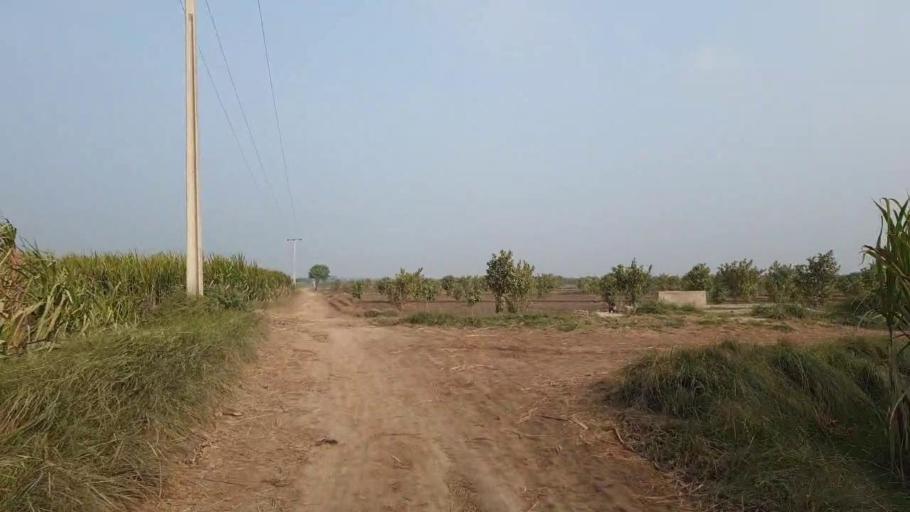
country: PK
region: Sindh
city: Tando Muhammad Khan
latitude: 25.1489
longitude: 68.5887
